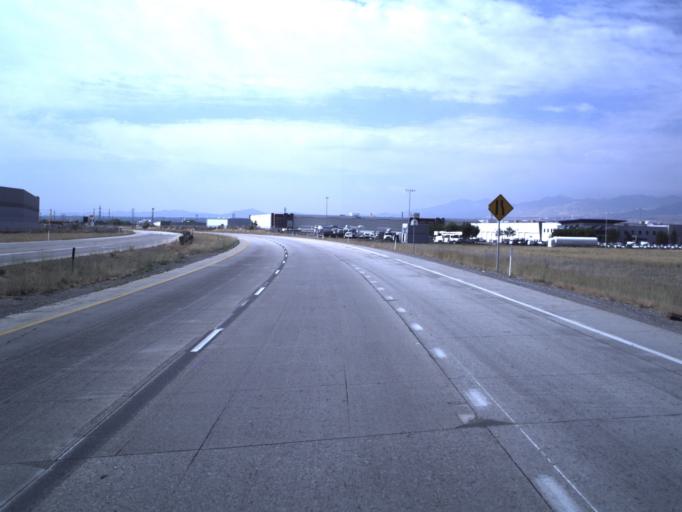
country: US
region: Utah
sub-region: Salt Lake County
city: West Valley City
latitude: 40.7427
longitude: -111.9900
